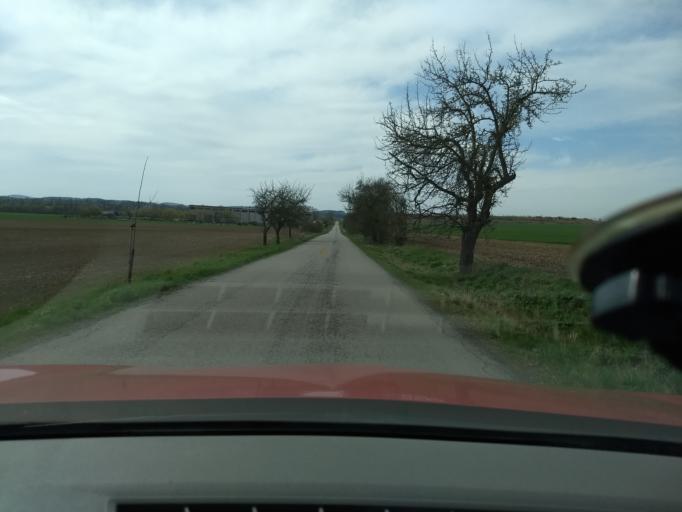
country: CZ
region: Central Bohemia
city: Rudna
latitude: 50.0507
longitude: 14.2124
